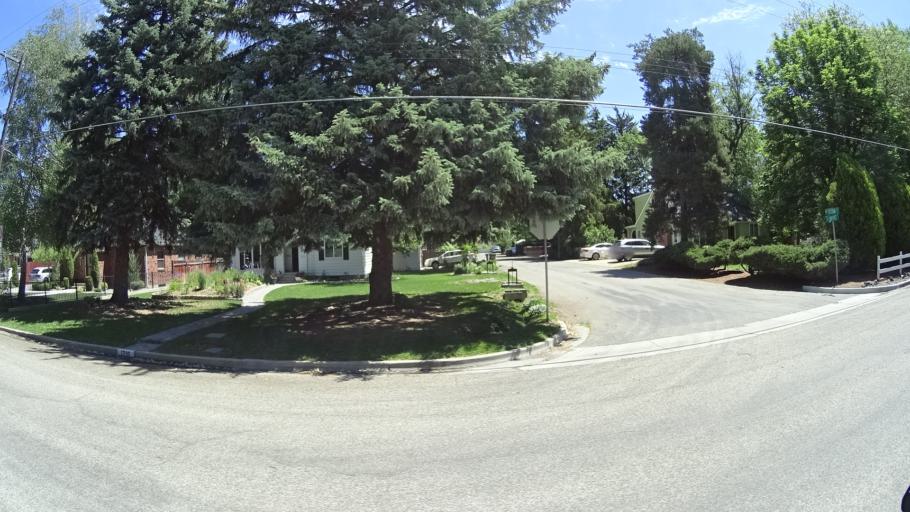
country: US
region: Idaho
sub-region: Ada County
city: Boise
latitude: 43.5927
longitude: -116.2236
